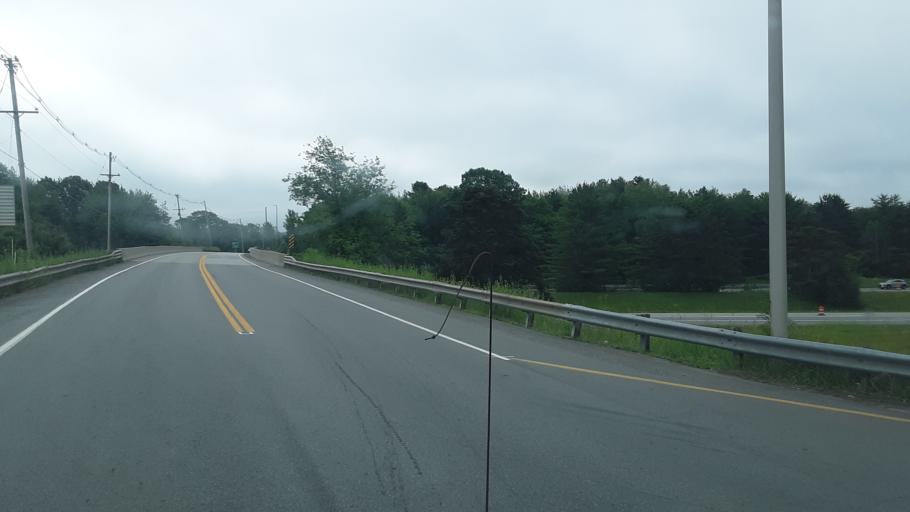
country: US
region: Maine
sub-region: Penobscot County
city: Hampden
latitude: 44.7744
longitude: -68.8602
